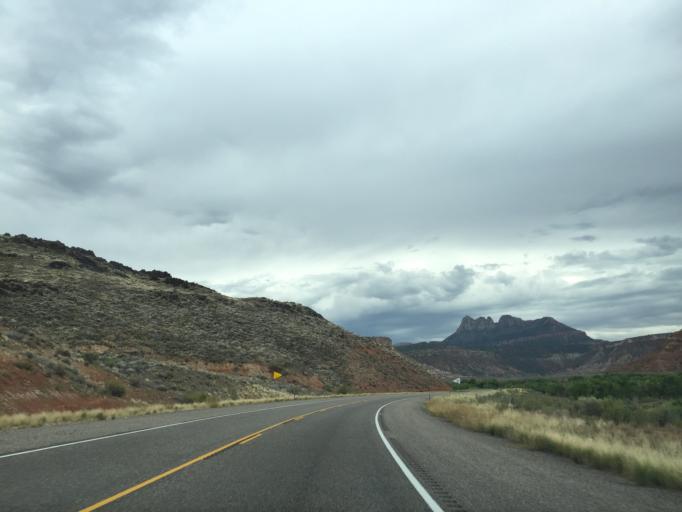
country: US
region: Utah
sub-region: Washington County
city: LaVerkin
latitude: 37.1774
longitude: -113.1158
